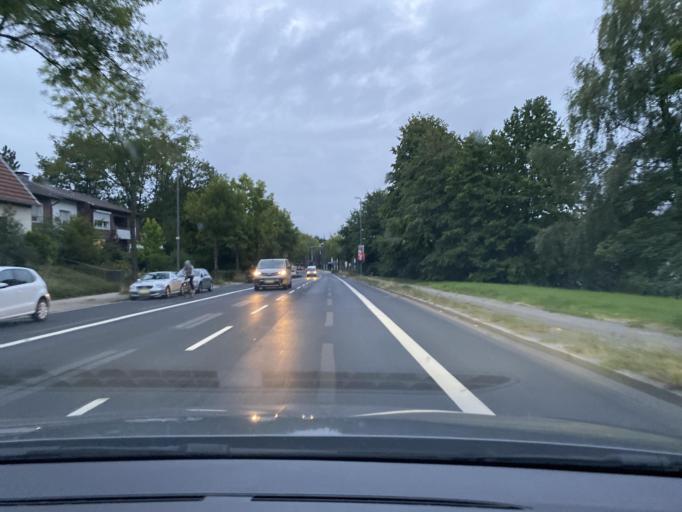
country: DE
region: North Rhine-Westphalia
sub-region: Regierungsbezirk Arnsberg
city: Bochum
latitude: 51.4387
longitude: 7.2072
